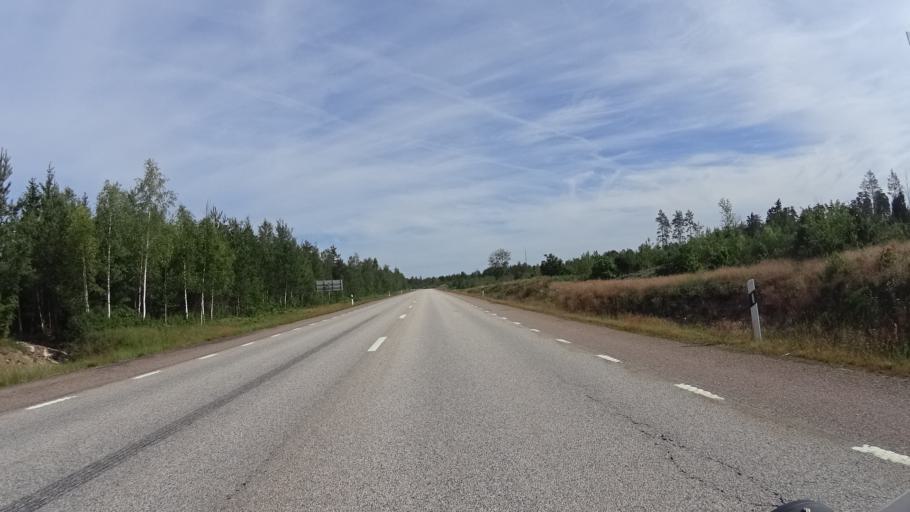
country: SE
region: Kalmar
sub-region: Oskarshamns Kommun
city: Oskarshamn
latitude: 57.4846
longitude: 16.5181
